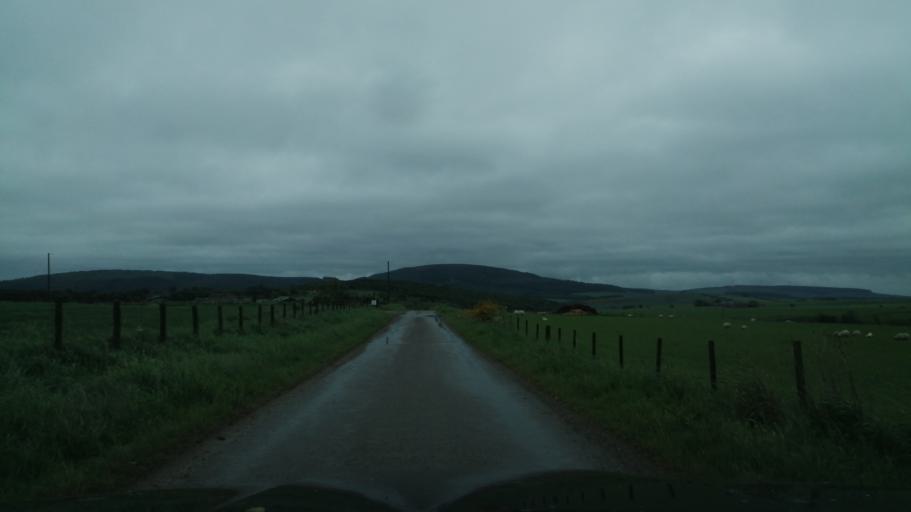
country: GB
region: Scotland
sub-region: Moray
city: Keith
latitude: 57.5750
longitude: -2.8604
